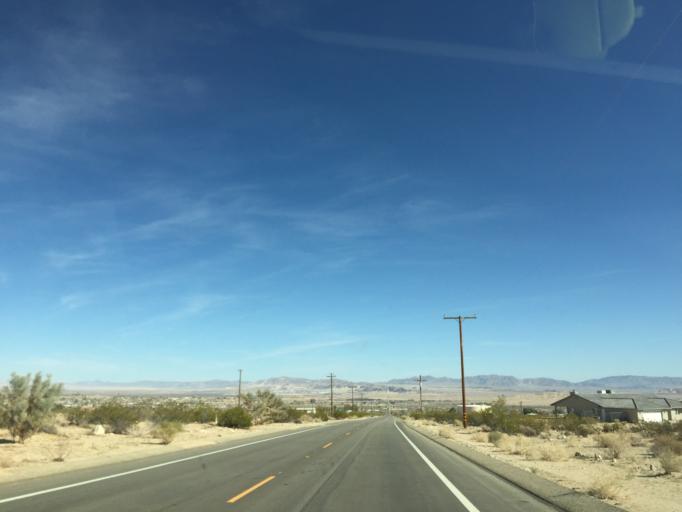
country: US
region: California
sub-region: San Bernardino County
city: Twentynine Palms
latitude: 34.1054
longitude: -116.0367
